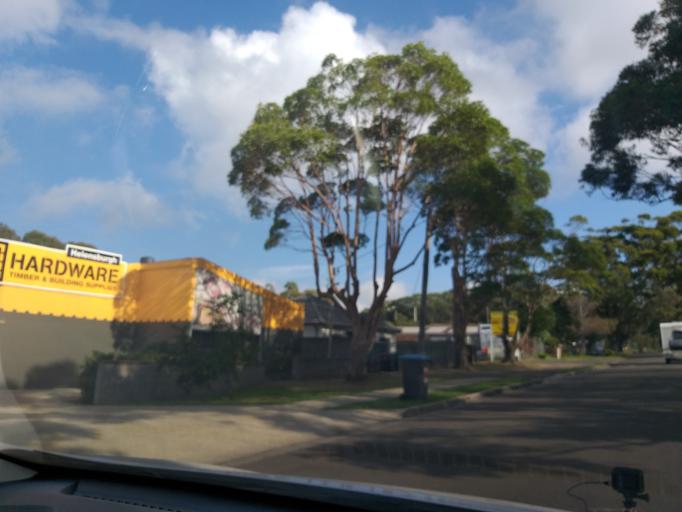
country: AU
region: New South Wales
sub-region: Wollongong
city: Helensburgh
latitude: -34.1956
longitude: 150.9752
